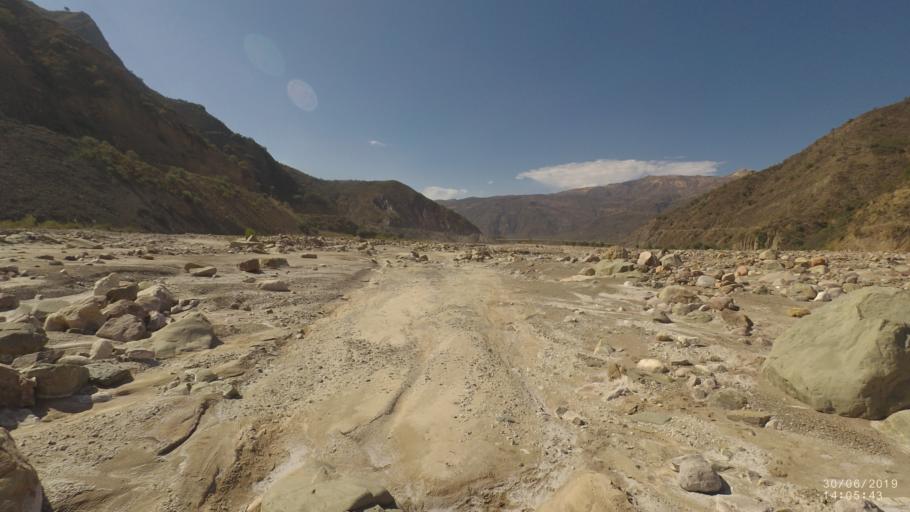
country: BO
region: Cochabamba
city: Irpa Irpa
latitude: -17.8048
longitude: -66.3572
